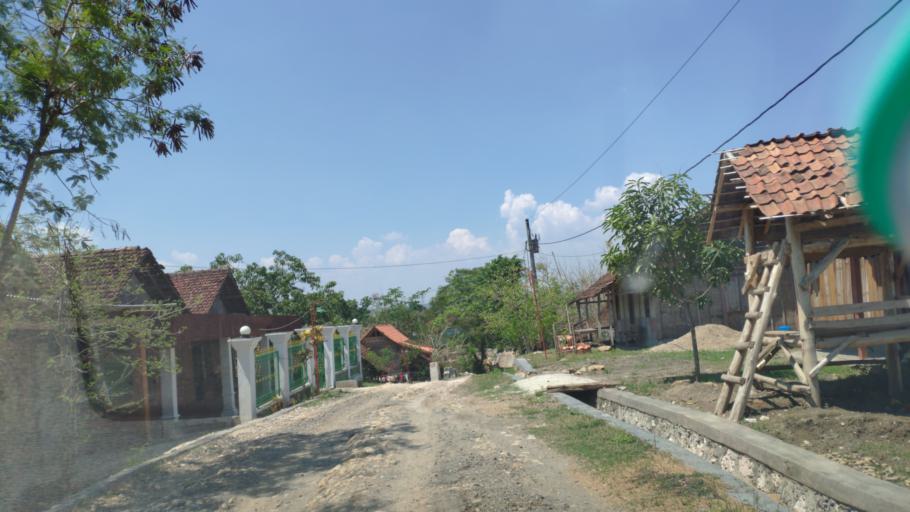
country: ID
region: Central Java
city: Galuk
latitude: -7.1070
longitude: 111.5025
